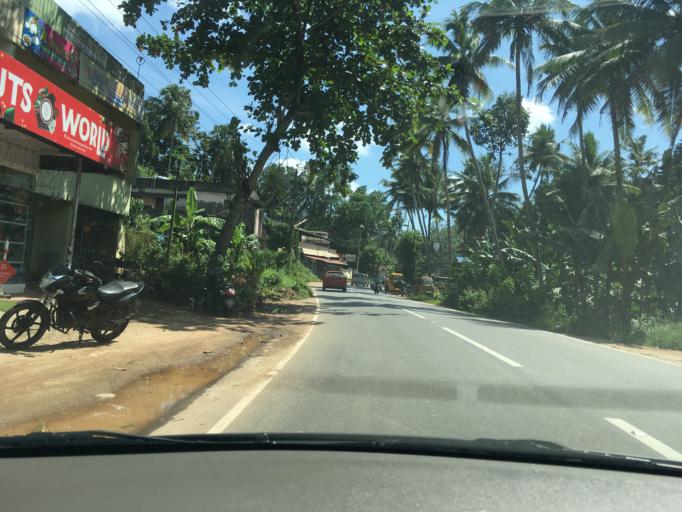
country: IN
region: Kerala
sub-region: Thiruvananthapuram
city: Nedumangad
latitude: 8.5767
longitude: 76.9958
